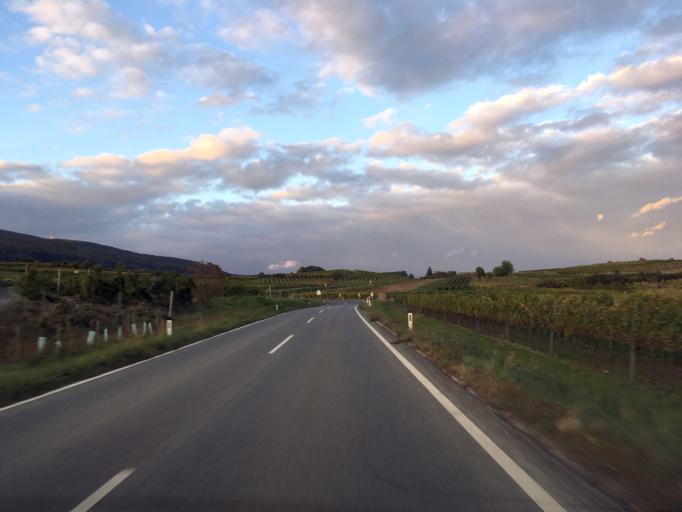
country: AT
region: Lower Austria
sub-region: Politischer Bezirk Baden
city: Pfaffstatten
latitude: 48.0233
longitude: 16.2585
